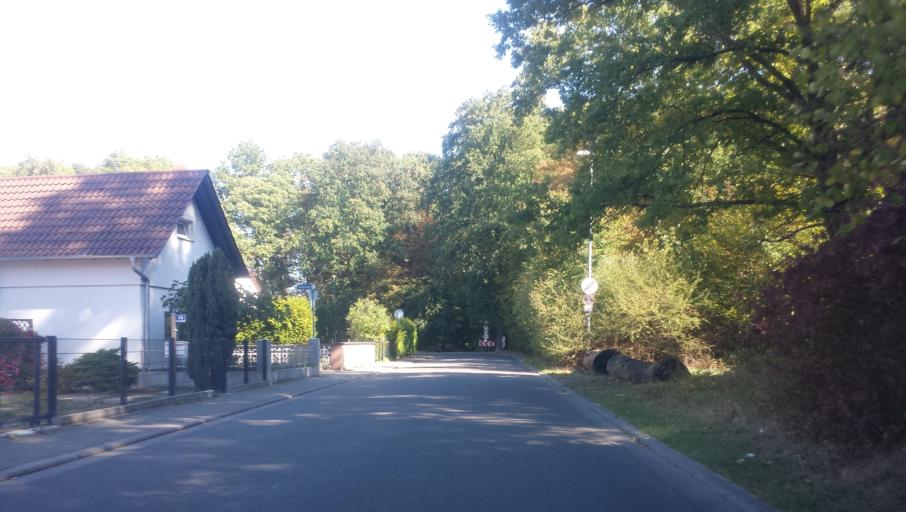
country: DE
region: Rheinland-Pfalz
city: Schifferstadt
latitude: 49.3792
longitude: 8.3952
